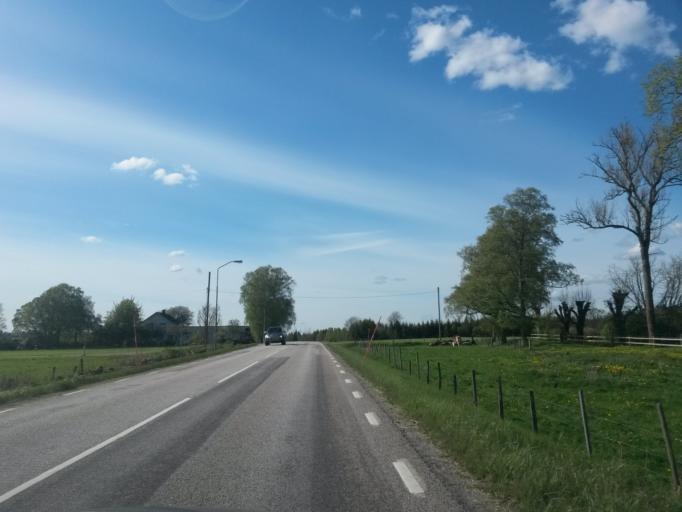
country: SE
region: Vaestra Goetaland
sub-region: Herrljunga Kommun
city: Herrljunga
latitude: 57.9505
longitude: 13.0054
